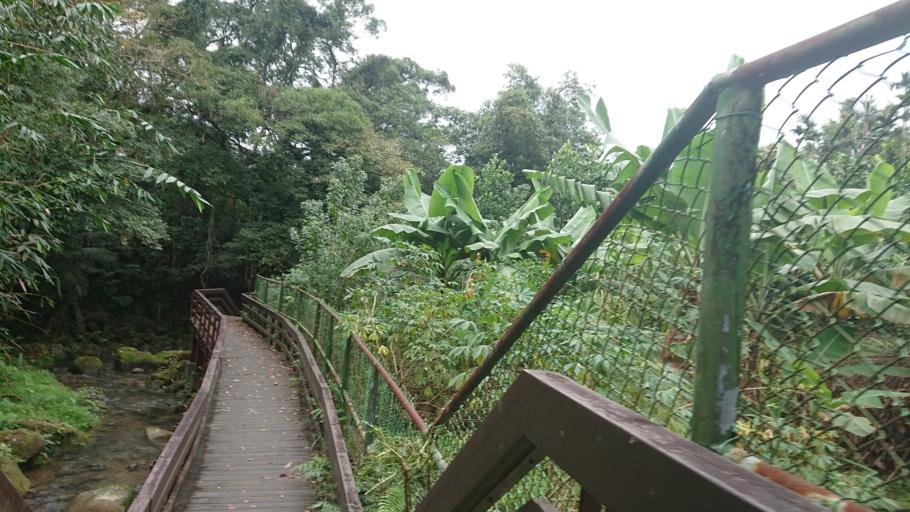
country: TW
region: Taipei
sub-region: Taipei
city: Banqiao
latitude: 24.9505
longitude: 121.4483
